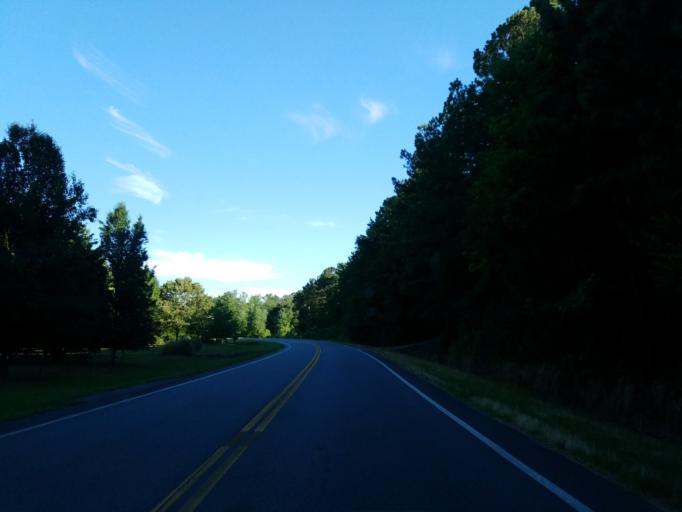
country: US
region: Georgia
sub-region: Gordon County
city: Calhoun
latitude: 34.5983
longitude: -85.0421
